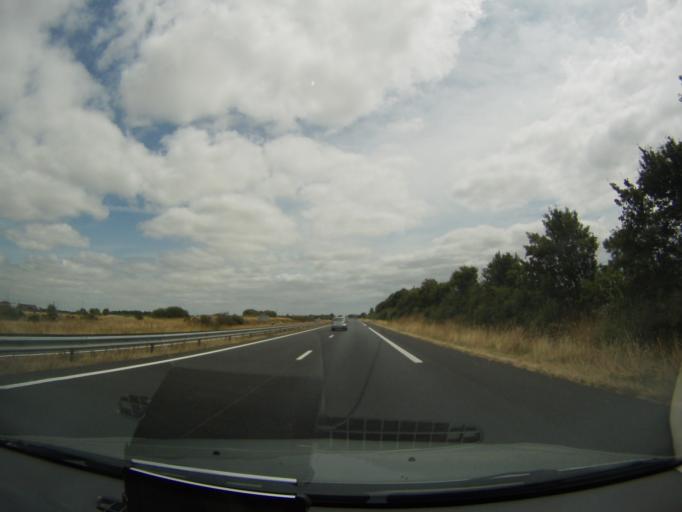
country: FR
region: Pays de la Loire
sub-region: Departement de Maine-et-Loire
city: Saint-Germain-sur-Moine
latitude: 47.1247
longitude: -1.1107
